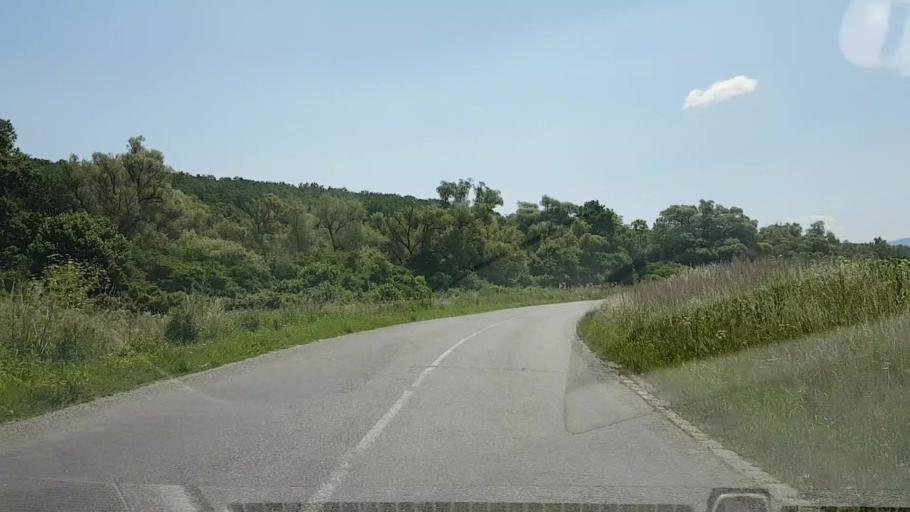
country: RO
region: Brasov
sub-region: Comuna Cincu
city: Cincu
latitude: 45.8775
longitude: 24.8172
